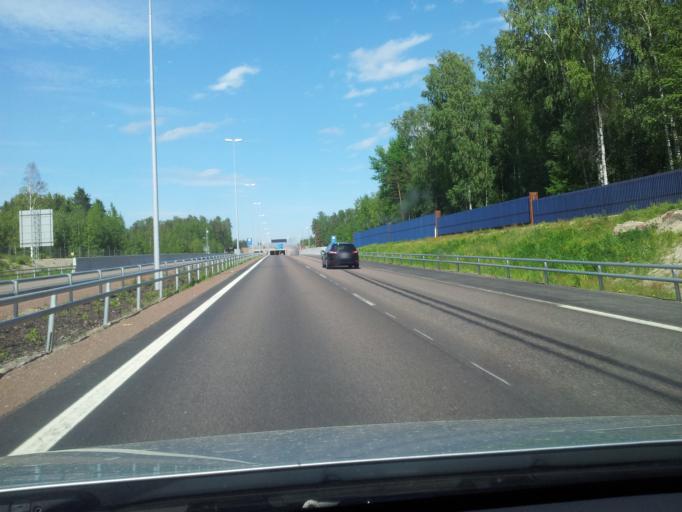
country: FI
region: Kymenlaakso
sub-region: Kotka-Hamina
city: Hamina
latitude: 60.5915
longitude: 27.1639
